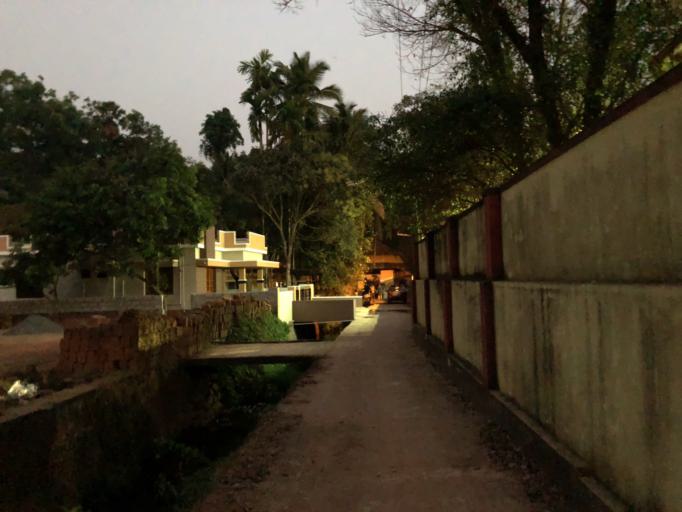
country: IN
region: Karnataka
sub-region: Dakshina Kannada
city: Mangalore
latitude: 12.8729
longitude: 74.8907
